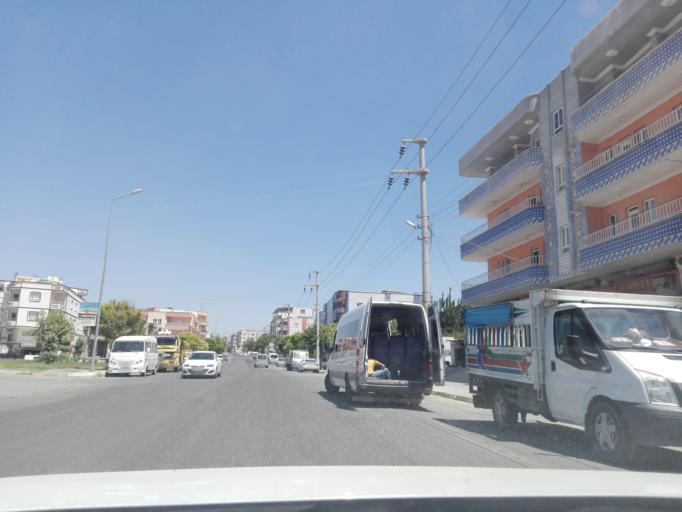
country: TR
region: Batman
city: Batman
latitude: 37.8864
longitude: 41.1424
